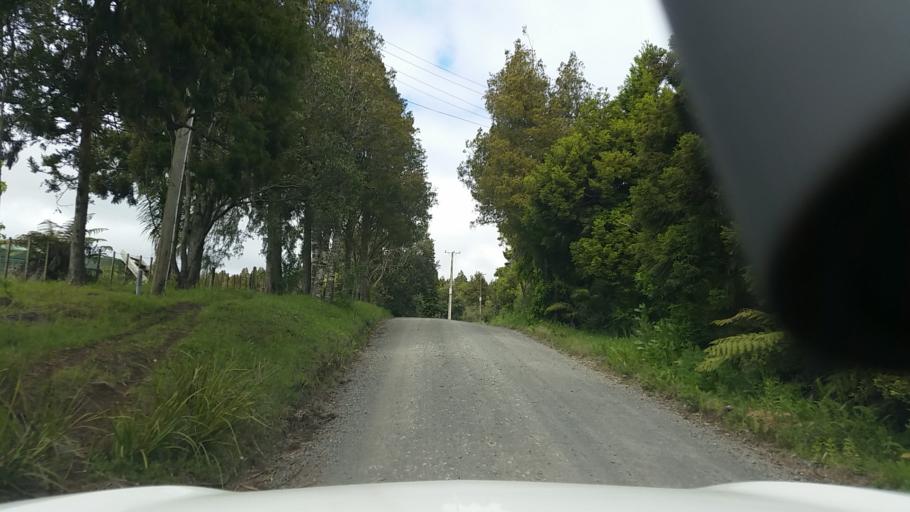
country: NZ
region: Auckland
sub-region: Auckland
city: Muriwai Beach
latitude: -36.8462
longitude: 174.5102
